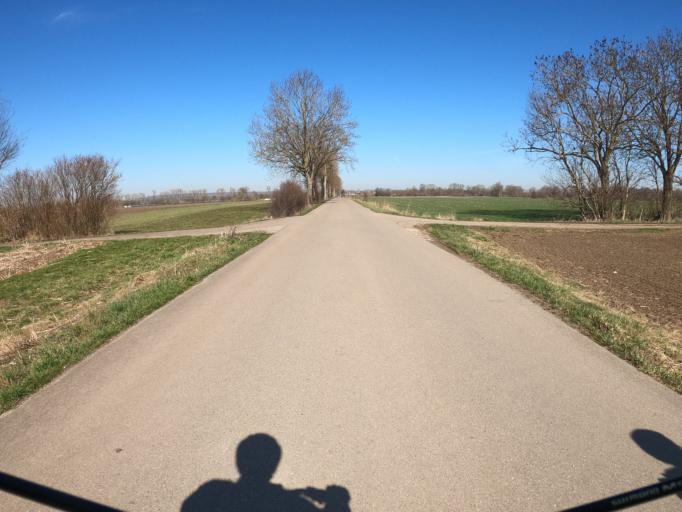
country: DE
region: Baden-Wuerttemberg
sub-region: Tuebingen Region
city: Langenau
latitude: 48.4667
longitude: 10.1418
